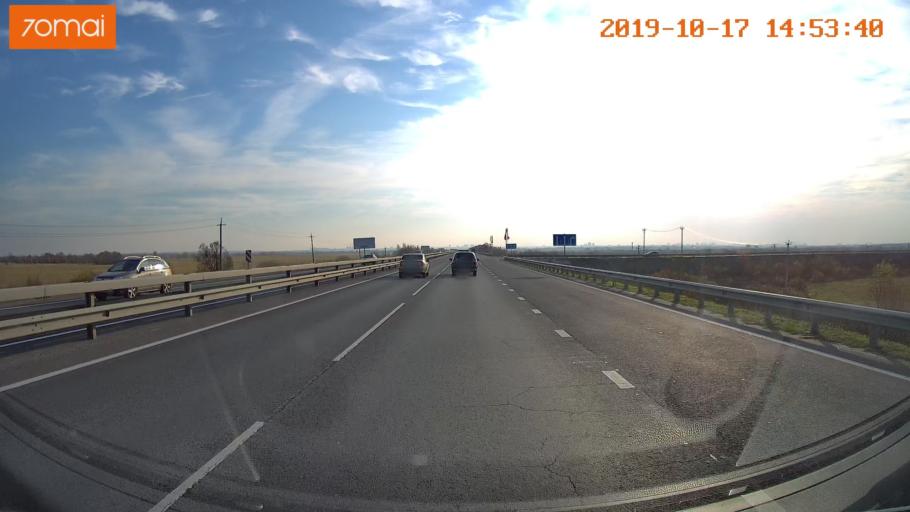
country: RU
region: Rjazan
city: Polyany
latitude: 54.6910
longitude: 39.8372
